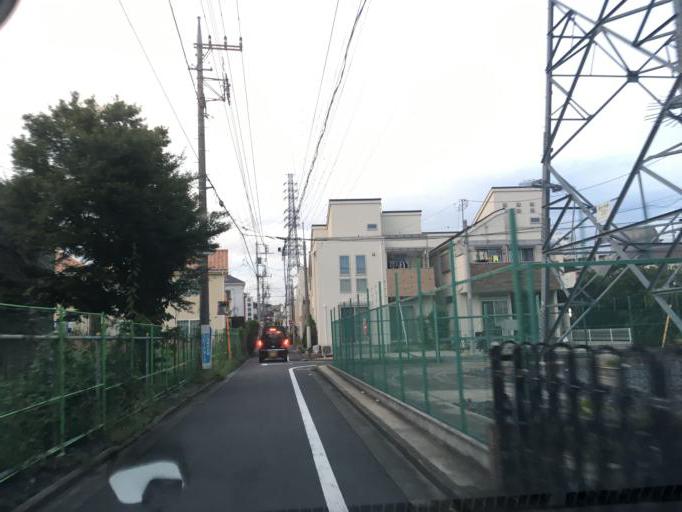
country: JP
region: Tokyo
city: Kokubunji
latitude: 35.6924
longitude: 139.4560
